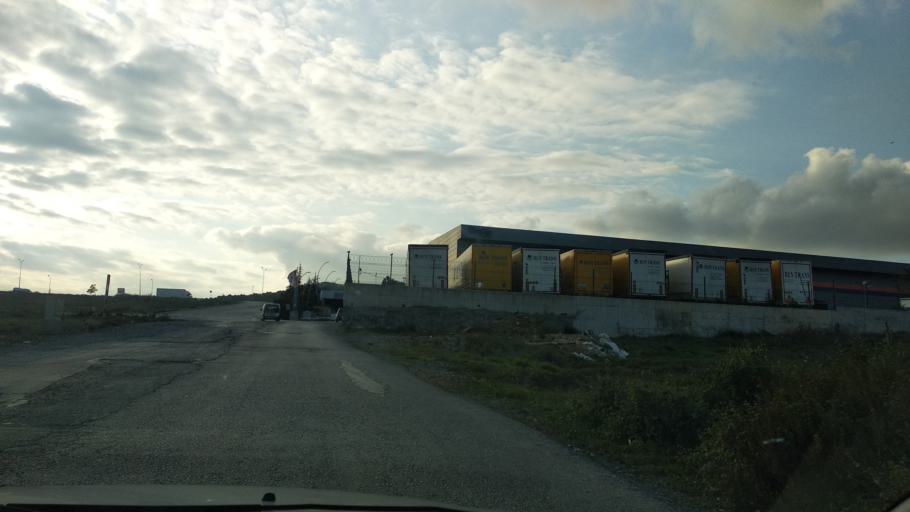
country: TR
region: Istanbul
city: Icmeler
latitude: 40.9204
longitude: 29.3451
